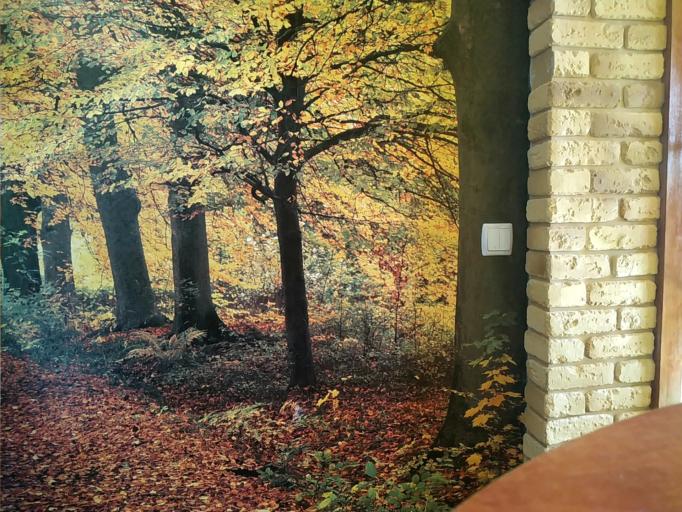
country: RU
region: Jaroslavl
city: Kukoboy
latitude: 58.8524
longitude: 39.7362
